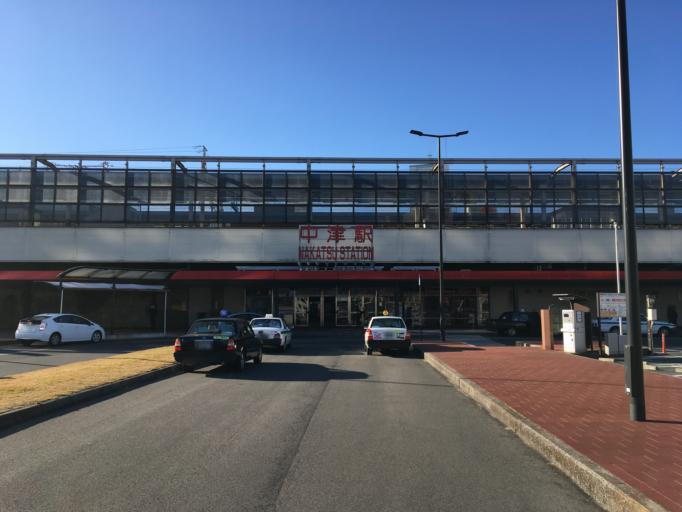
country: JP
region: Fukuoka
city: Nakatsu
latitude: 33.5998
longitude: 131.1908
